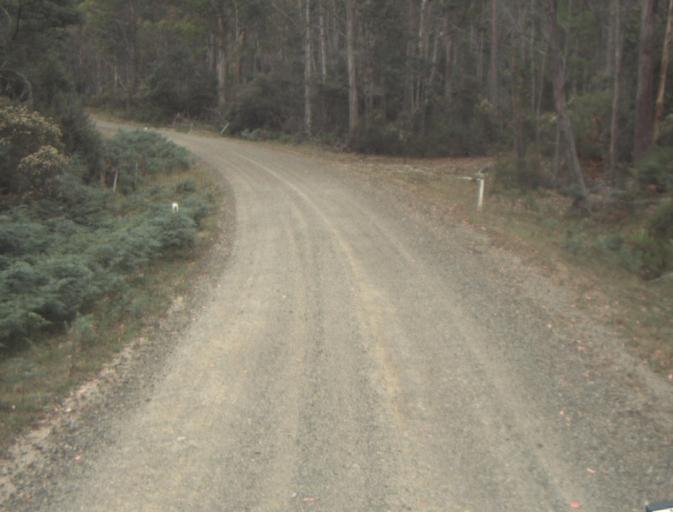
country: AU
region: Tasmania
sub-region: Dorset
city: Scottsdale
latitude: -41.4085
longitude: 147.5181
